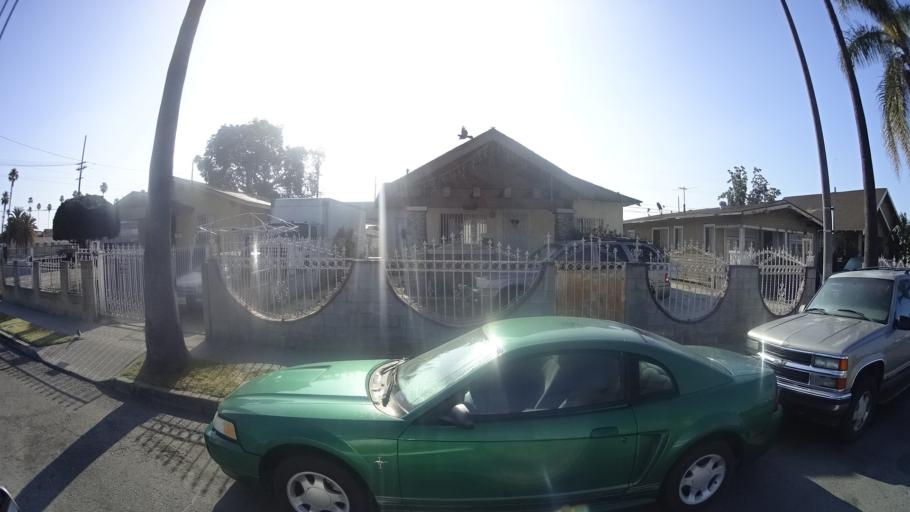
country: US
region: California
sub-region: Los Angeles County
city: Florence-Graham
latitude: 33.9885
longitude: -118.2838
